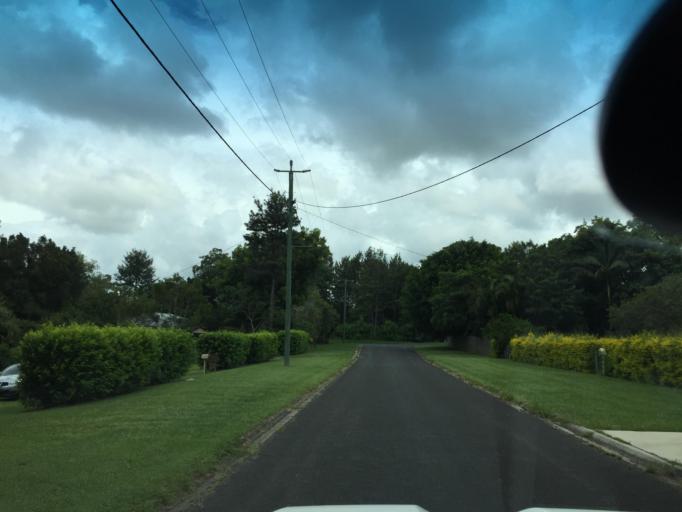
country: AU
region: Queensland
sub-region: Moreton Bay
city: Caboolture
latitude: -27.0435
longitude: 152.9230
